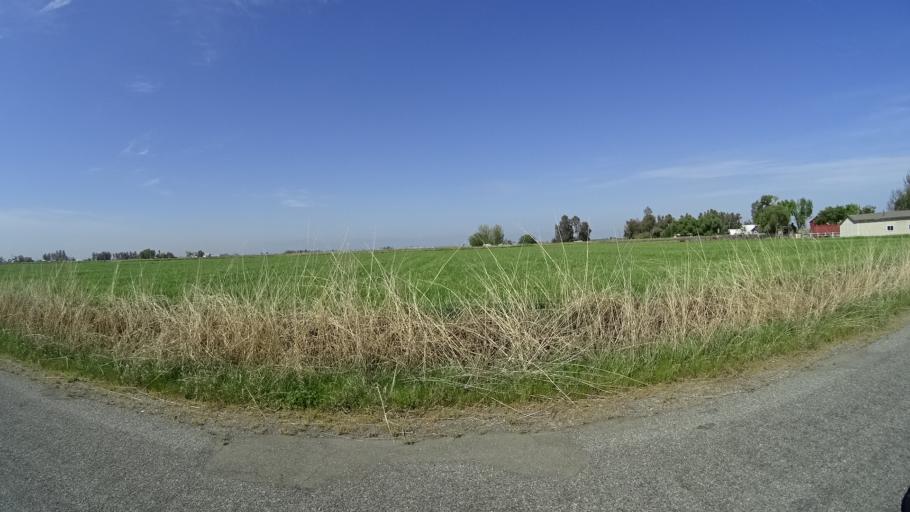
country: US
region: California
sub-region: Glenn County
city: Willows
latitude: 39.5926
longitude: -122.0558
